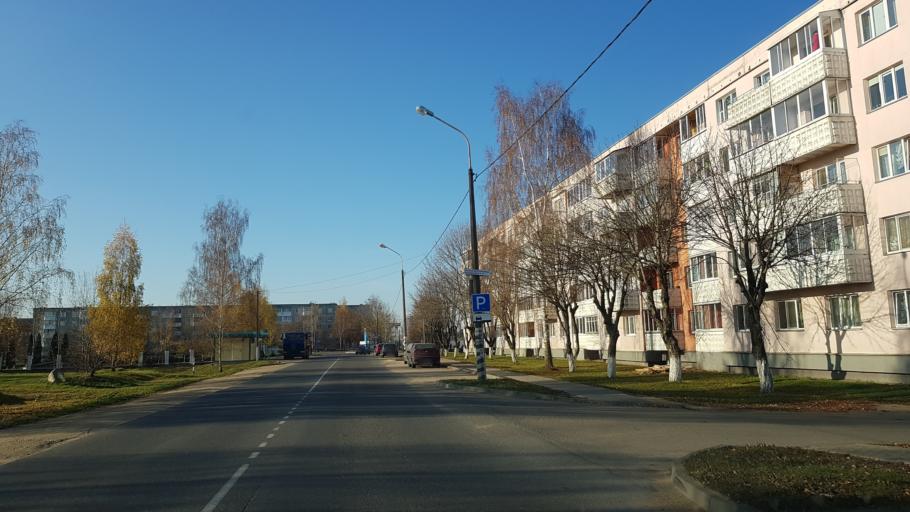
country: BY
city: Fanipol
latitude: 53.7384
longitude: 27.3187
